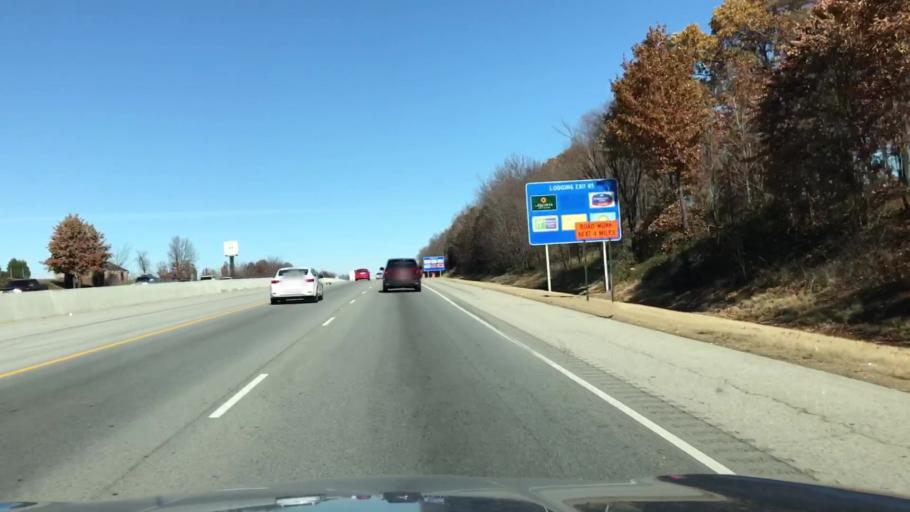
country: US
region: Arkansas
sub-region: Benton County
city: Bentonville
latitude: 36.3239
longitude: -94.1847
